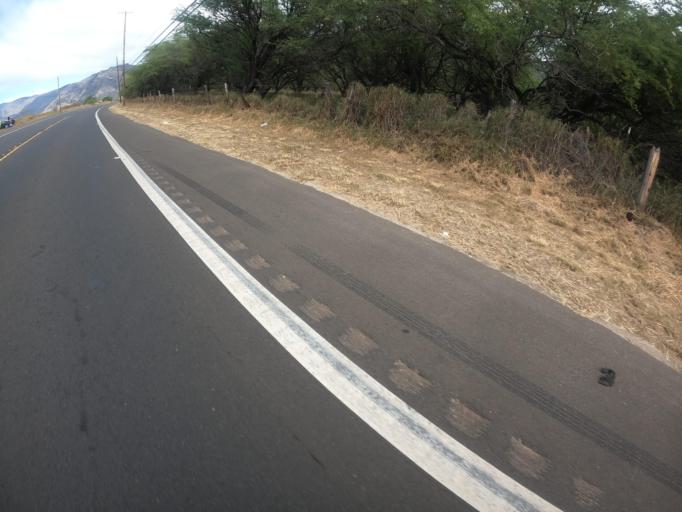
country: US
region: Hawaii
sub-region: Honolulu County
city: Makaha Valley
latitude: 21.5005
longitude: -158.2296
